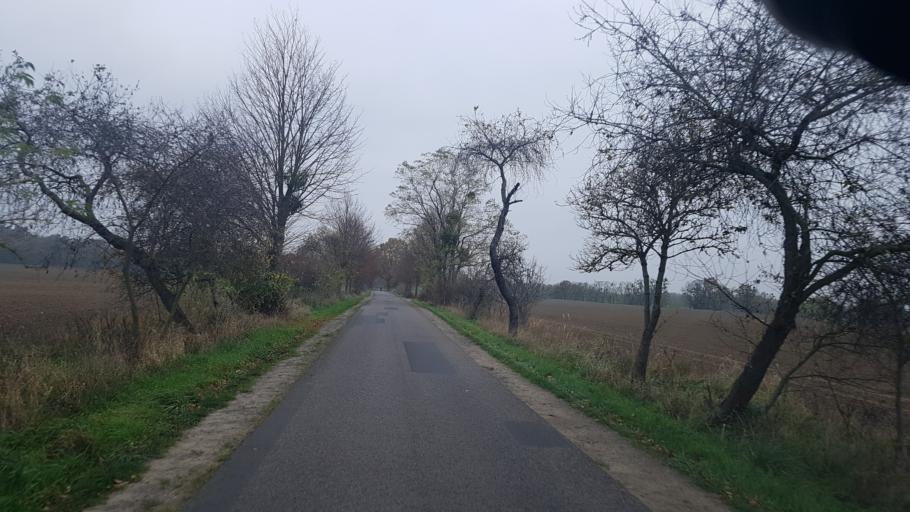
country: DE
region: Brandenburg
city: Lindow
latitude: 52.9417
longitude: 13.0584
